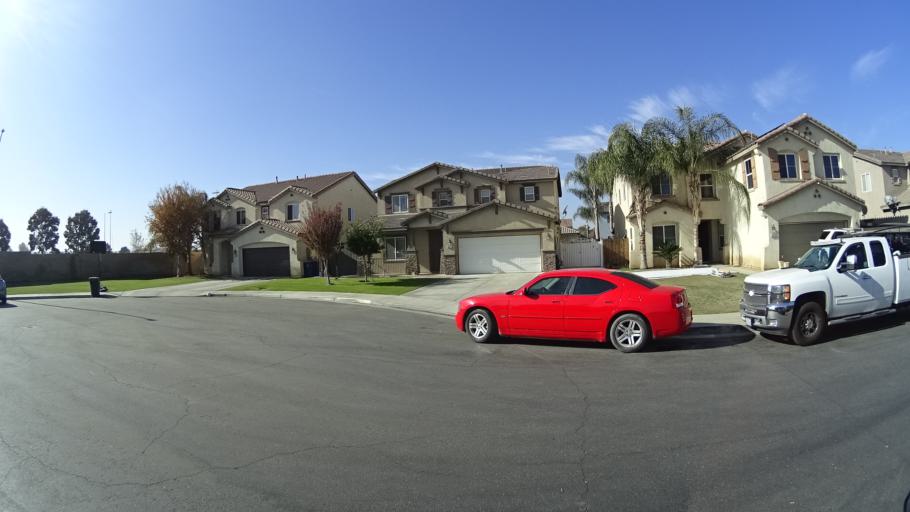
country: US
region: California
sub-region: Kern County
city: Greenfield
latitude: 35.2802
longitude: -119.0601
